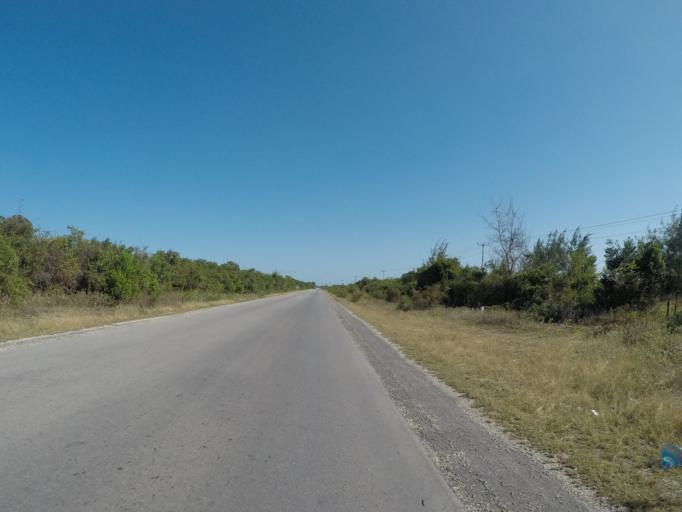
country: TZ
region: Zanzibar Central/South
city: Nganane
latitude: -6.2200
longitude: 39.5291
